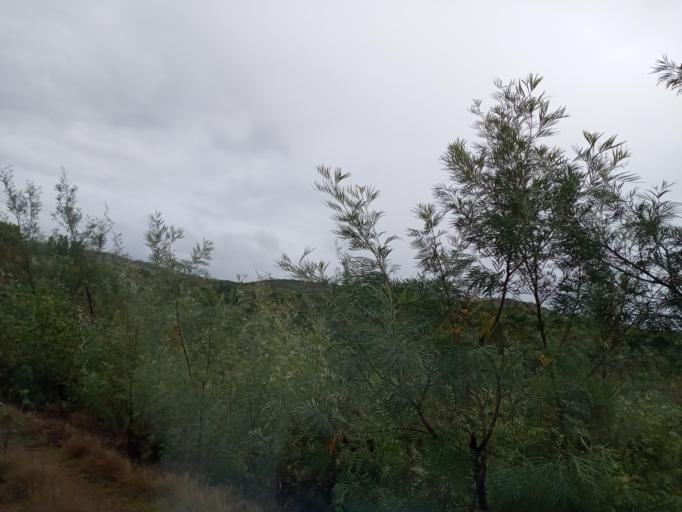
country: MG
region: Atsimo-Atsinanana
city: Vohipaho
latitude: -24.0000
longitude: 47.4049
